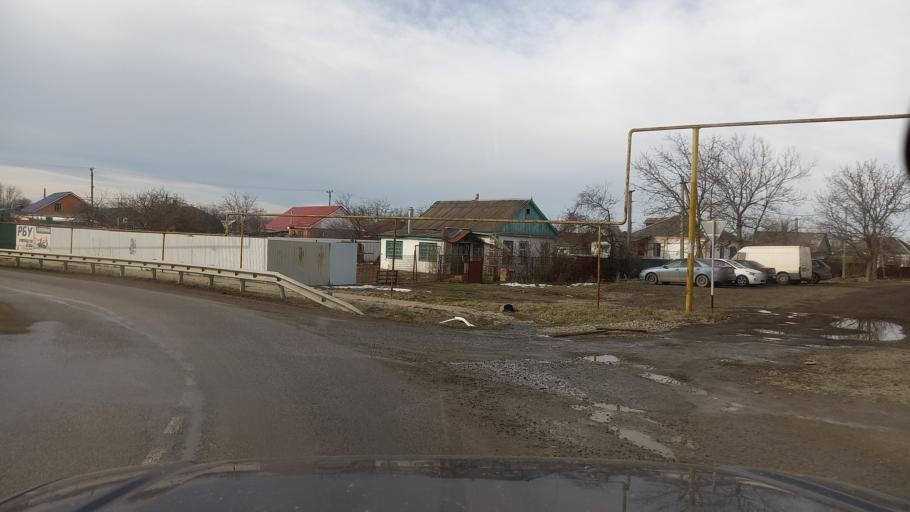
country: RU
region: Krasnodarskiy
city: Belorechensk
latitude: 44.7679
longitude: 39.9041
